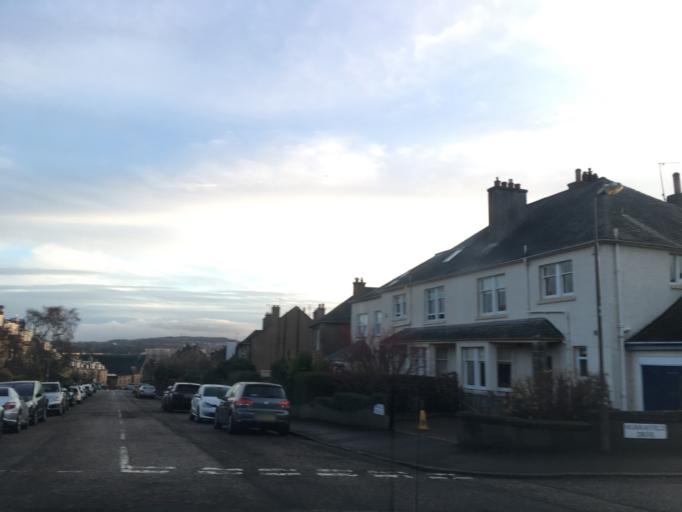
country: GB
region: Scotland
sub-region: Edinburgh
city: Colinton
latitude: 55.9480
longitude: -3.2433
